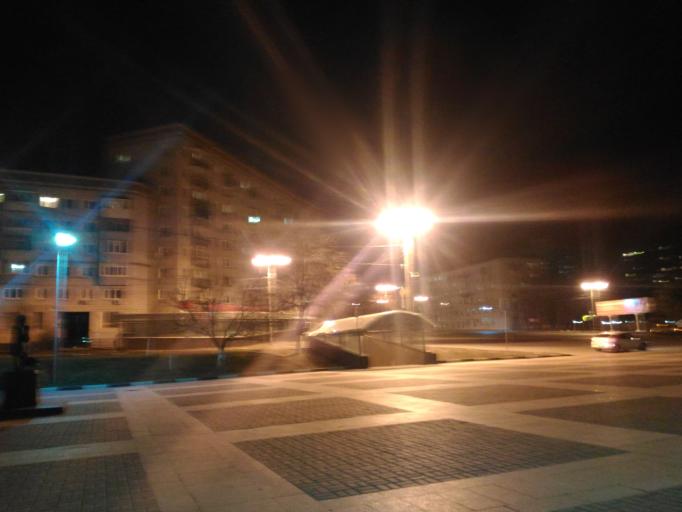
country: RU
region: Ulyanovsk
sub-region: Ulyanovskiy Rayon
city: Ulyanovsk
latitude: 54.3077
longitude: 48.3955
